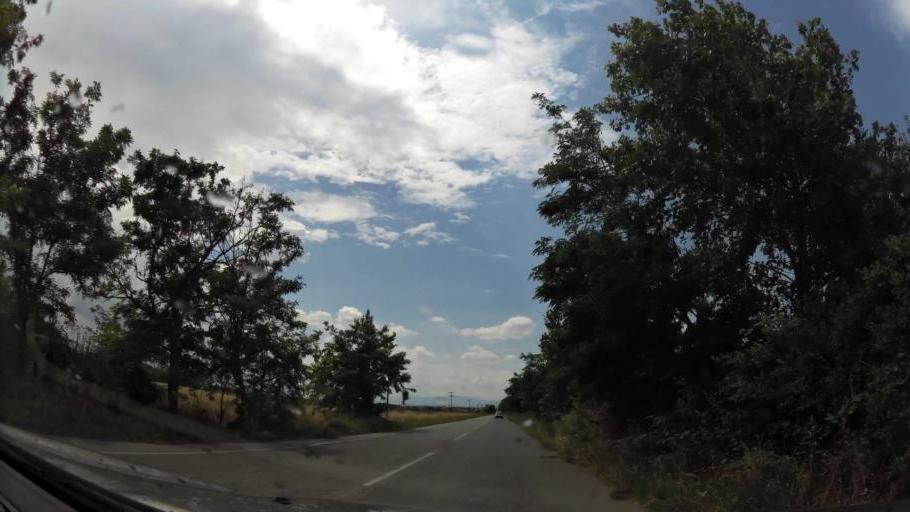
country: GR
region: Central Macedonia
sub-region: Nomos Pierias
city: Korinos
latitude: 40.3095
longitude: 22.6075
